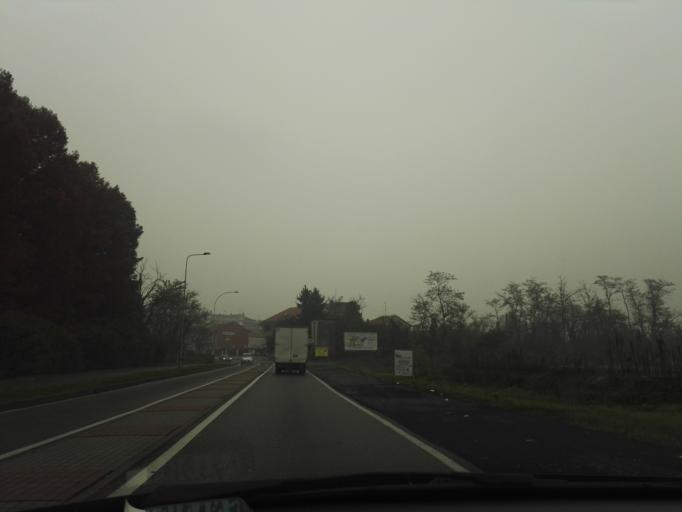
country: IT
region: Lombardy
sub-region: Citta metropolitana di Milano
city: Settimo Milanese
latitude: 45.4889
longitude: 9.0626
